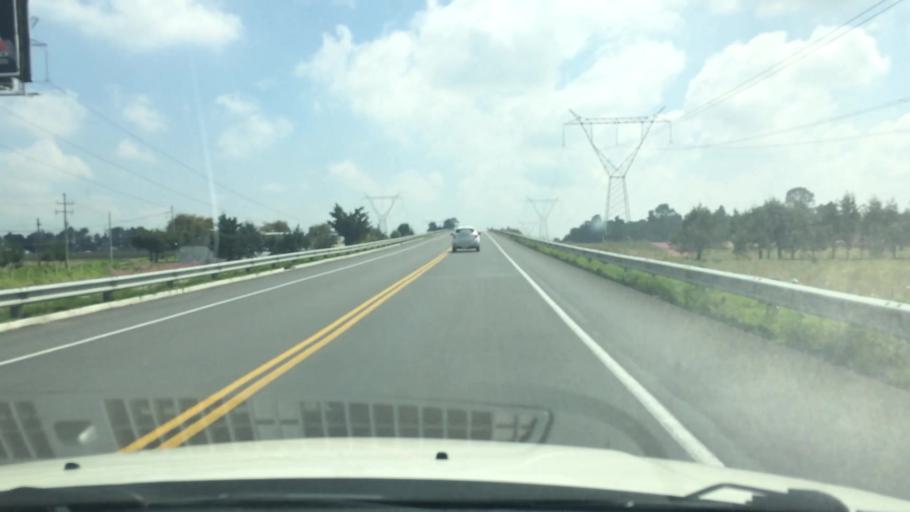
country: MX
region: Mexico
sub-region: Almoloya de Juarez
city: Fraccionamiento Colinas del Sol
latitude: 19.3866
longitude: -99.7441
